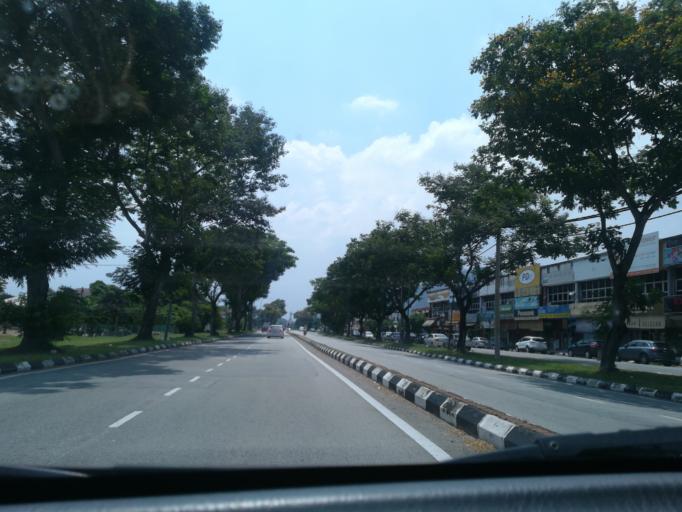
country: MY
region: Perak
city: Ipoh
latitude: 4.5807
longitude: 101.1273
